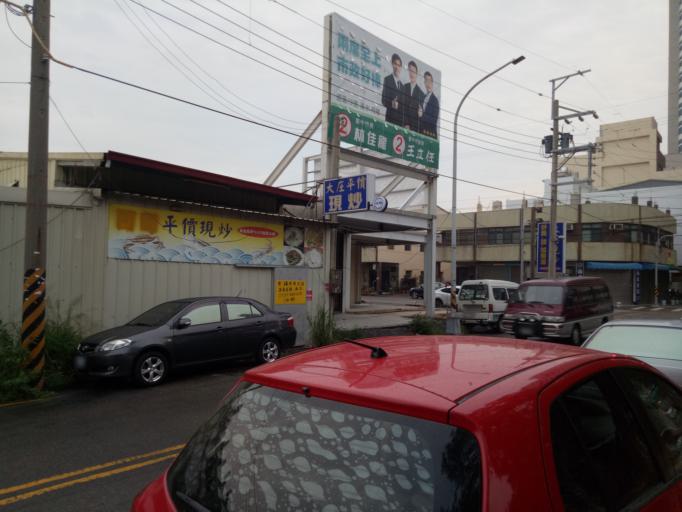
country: TW
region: Taiwan
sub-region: Taichung City
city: Taichung
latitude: 24.2459
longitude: 120.5419
